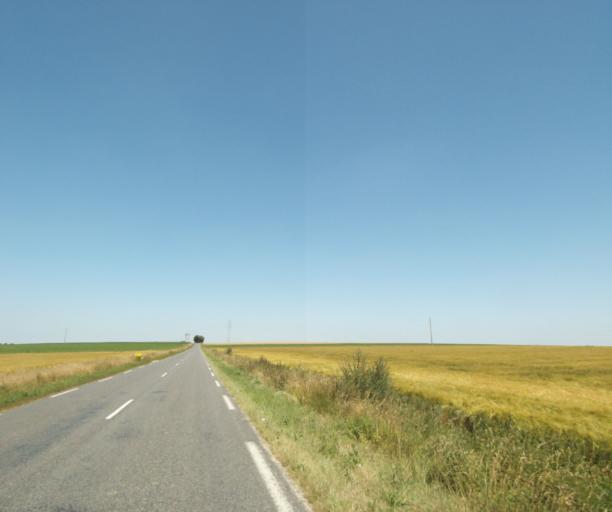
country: FR
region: Centre
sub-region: Departement du Loiret
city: Malesherbes
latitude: 48.3332
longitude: 2.4520
